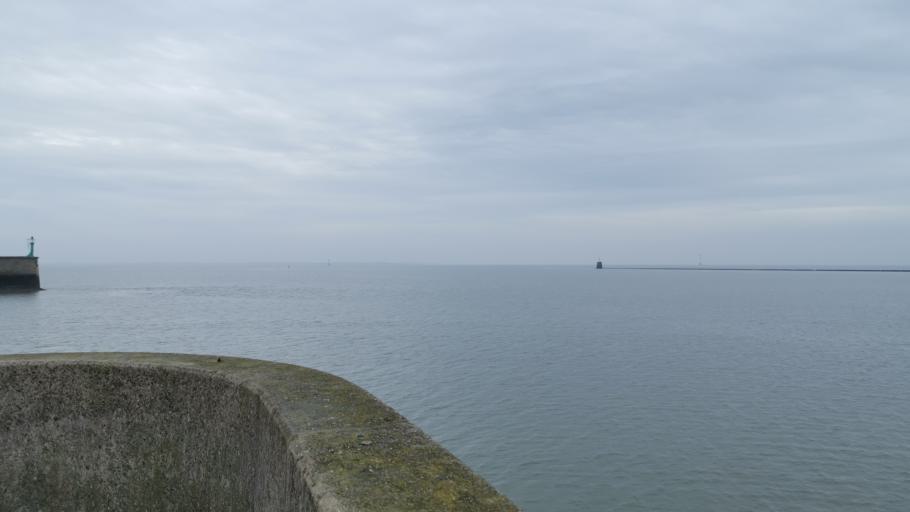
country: DE
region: Lower Saxony
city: Wilhelmshaven
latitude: 53.5133
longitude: 8.1528
